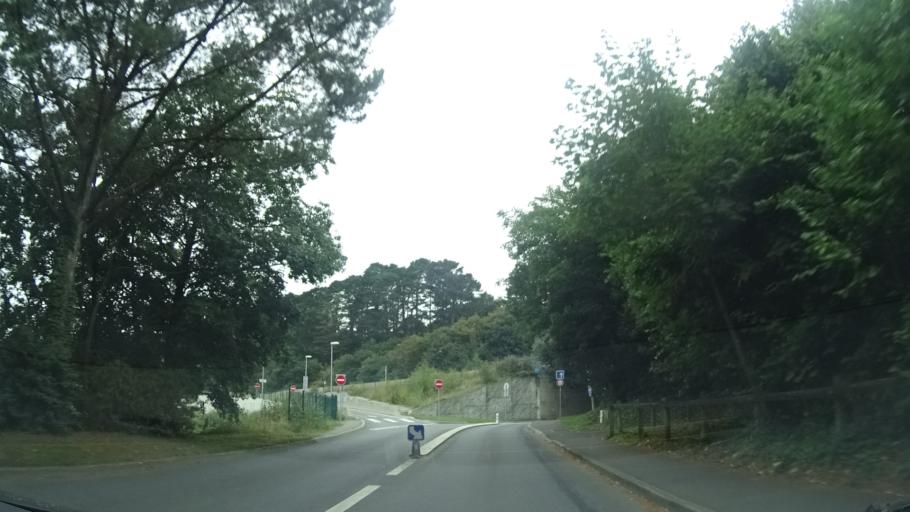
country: FR
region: Brittany
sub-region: Departement du Finistere
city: Brest
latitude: 48.3929
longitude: -4.4480
